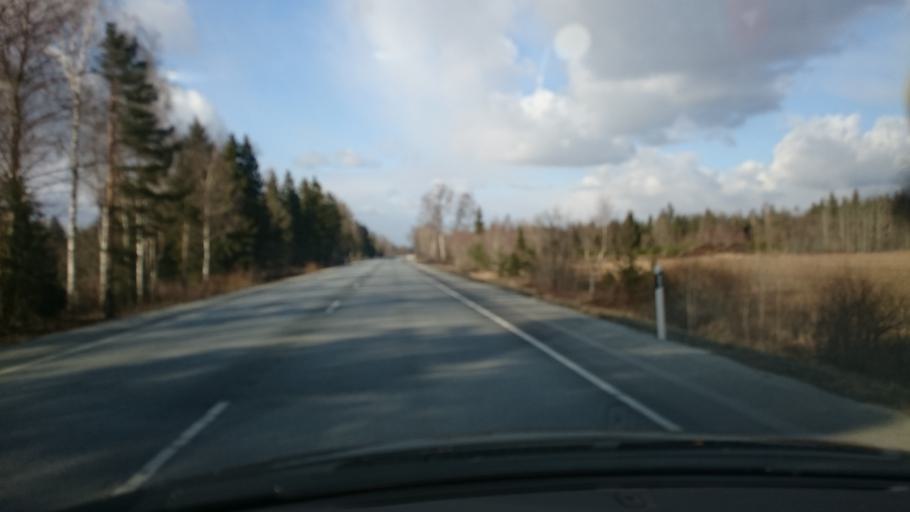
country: EE
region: Harju
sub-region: Nissi vald
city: Riisipere
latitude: 59.1418
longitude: 24.3313
